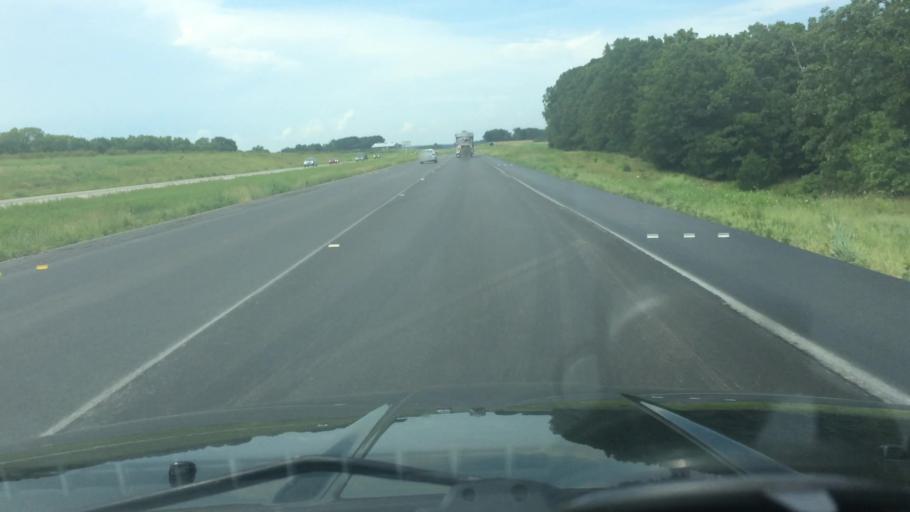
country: US
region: Missouri
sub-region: Saint Clair County
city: Osceola
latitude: 37.9710
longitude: -93.6464
